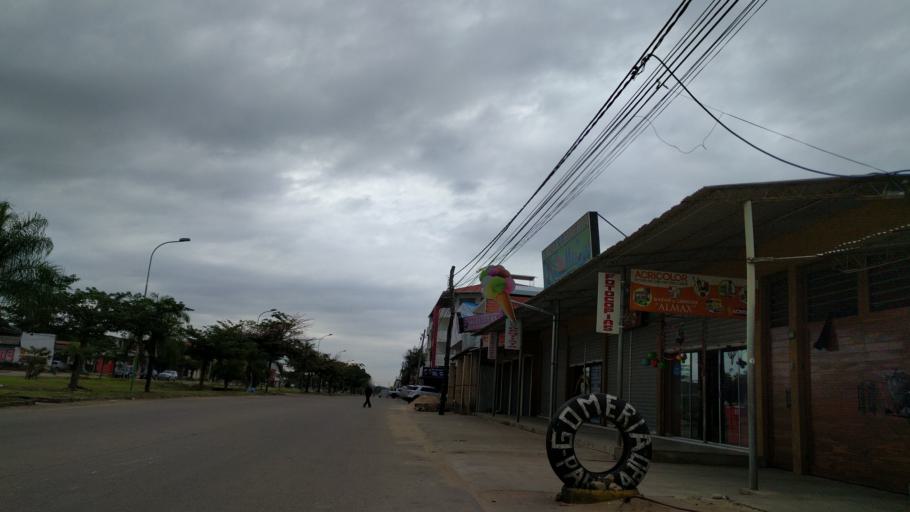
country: BO
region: Santa Cruz
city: Santa Cruz de la Sierra
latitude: -17.8153
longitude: -63.2231
